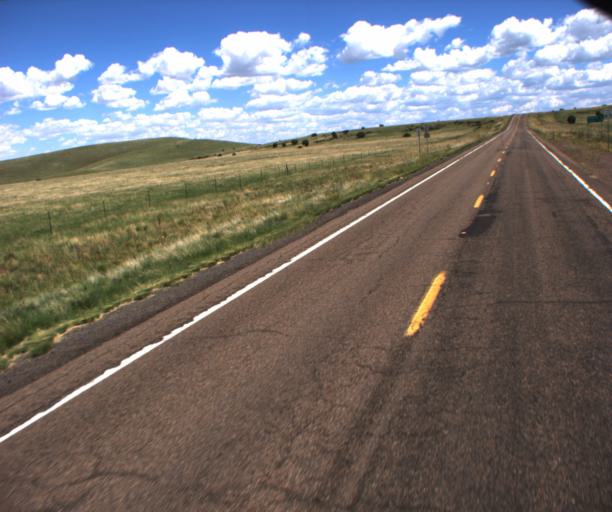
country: US
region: Arizona
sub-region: Apache County
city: Springerville
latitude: 34.2396
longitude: -109.5103
